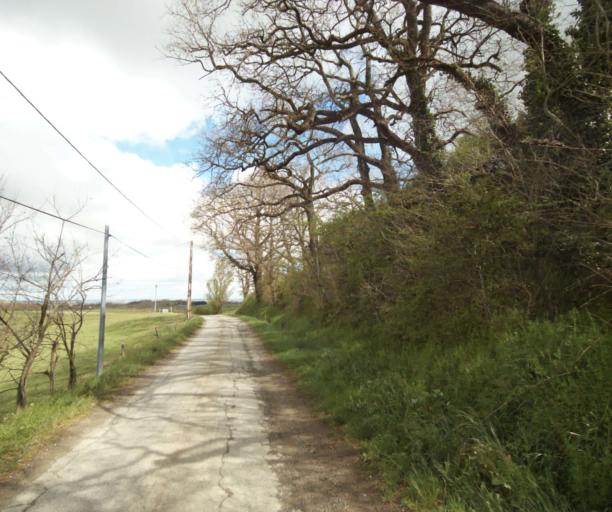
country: FR
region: Midi-Pyrenees
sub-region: Departement de l'Ariege
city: Saverdun
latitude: 43.1951
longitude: 1.5397
